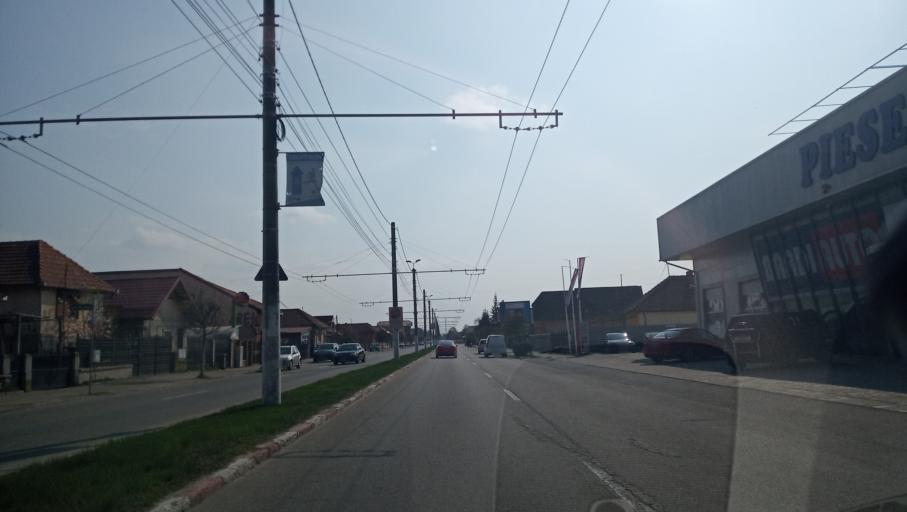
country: RO
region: Gorj
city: Targu Jiu
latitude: 45.0734
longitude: 23.2977
